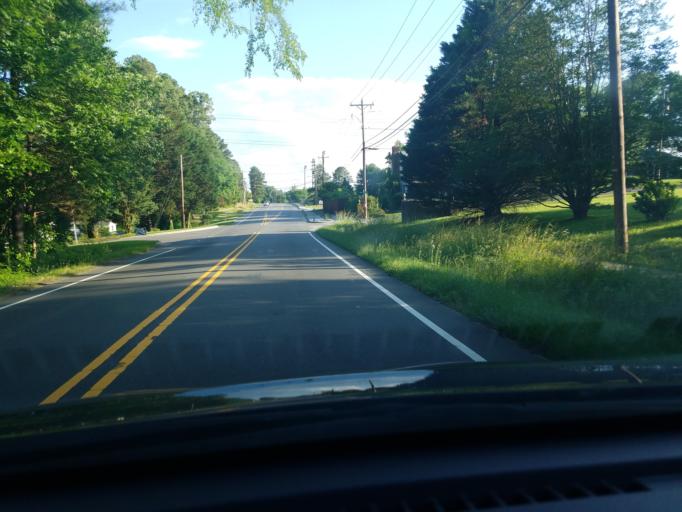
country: US
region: North Carolina
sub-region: Durham County
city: Durham
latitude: 35.9269
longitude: -78.9607
